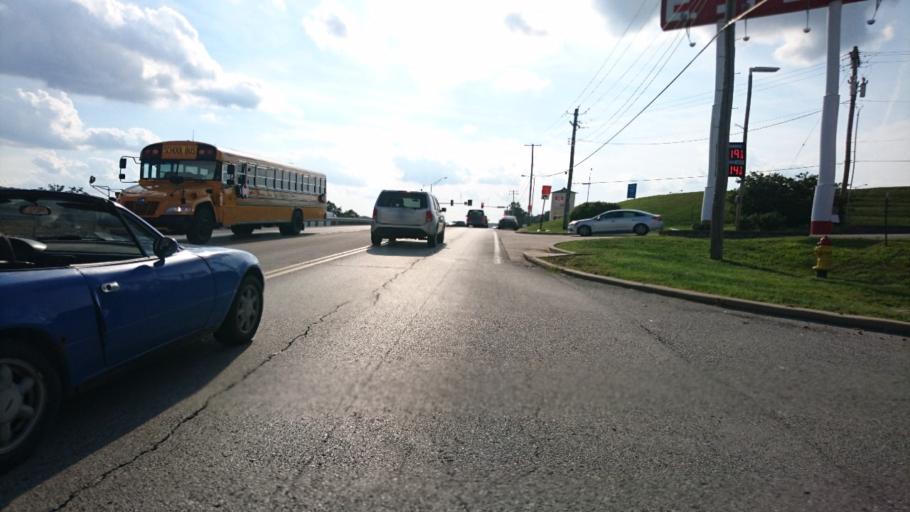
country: US
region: Missouri
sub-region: Saint Louis County
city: Eureka
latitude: 38.5068
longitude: -90.6321
